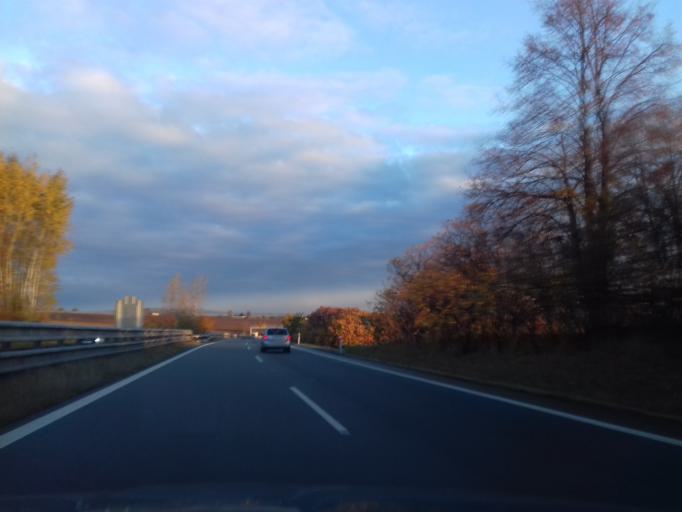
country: CZ
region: Olomoucky
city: Otaslavice
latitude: 49.3831
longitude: 17.0973
